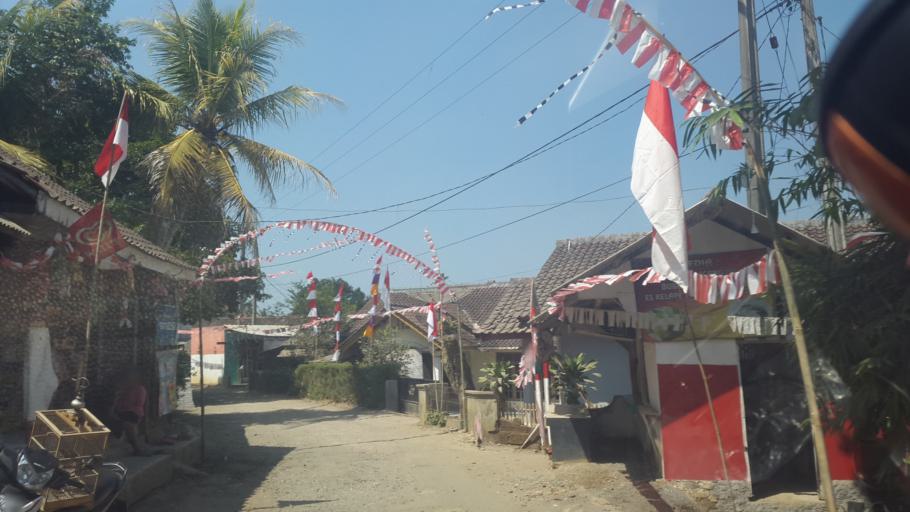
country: ID
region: West Java
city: Gunungkalong
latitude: -6.9340
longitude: 106.7789
